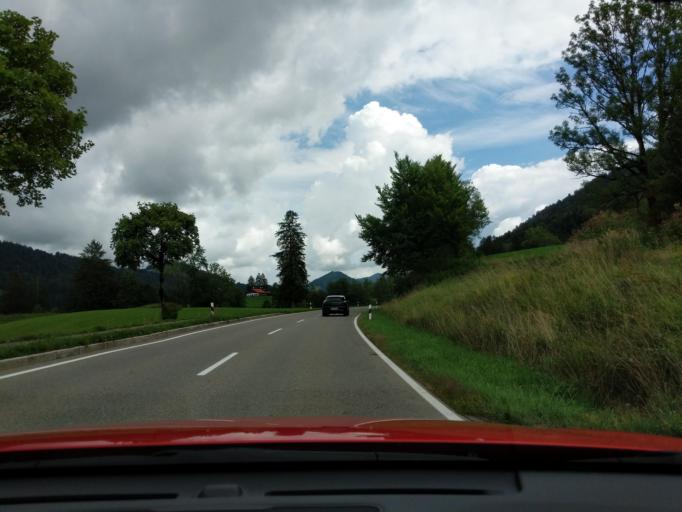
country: AT
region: Vorarlberg
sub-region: Politischer Bezirk Bregenz
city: Riefensberg
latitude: 47.5236
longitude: 9.9737
